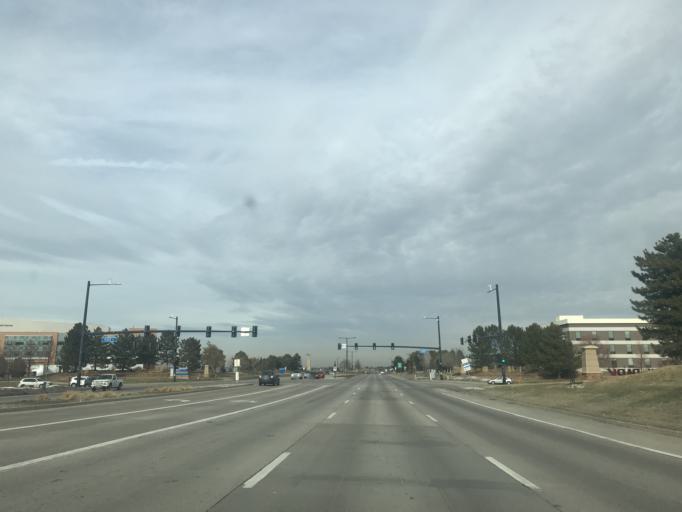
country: US
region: Colorado
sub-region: Douglas County
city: Highlands Ranch
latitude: 39.5547
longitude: -105.0081
